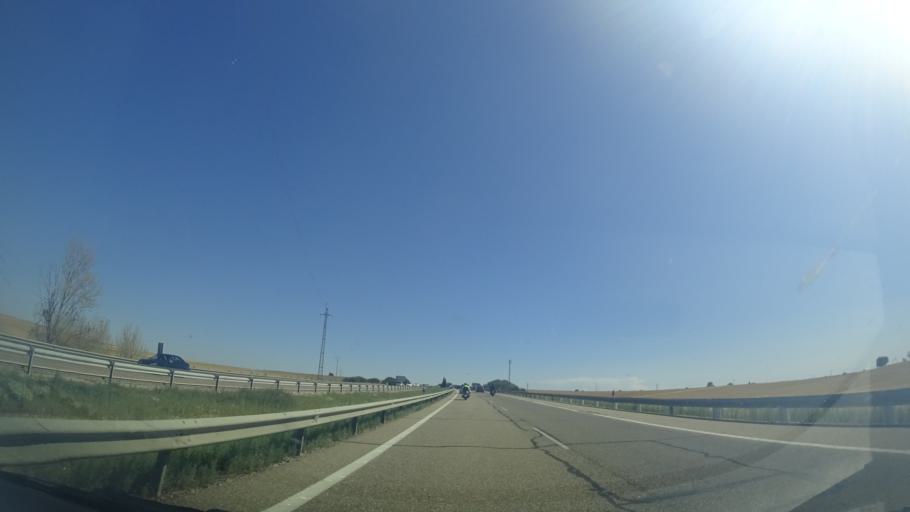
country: ES
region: Castille and Leon
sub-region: Provincia de Zamora
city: Cerecinos de Campos
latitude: 41.8955
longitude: -5.4723
